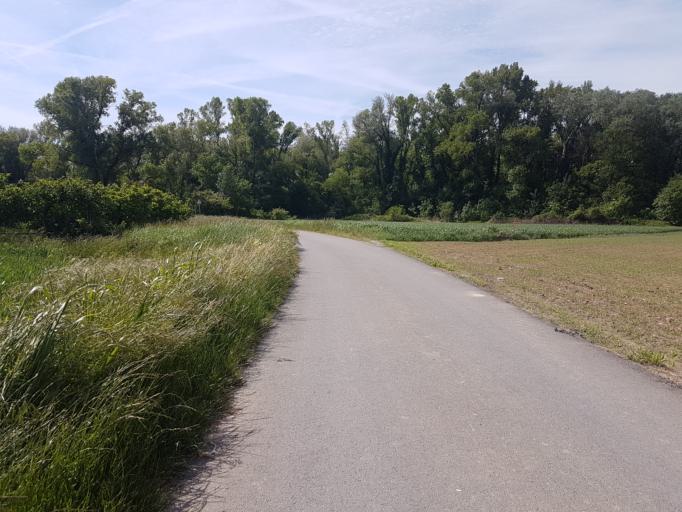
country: FR
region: Rhone-Alpes
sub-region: Departement de l'Ardeche
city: Le Pouzin
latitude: 44.7322
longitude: 4.7565
